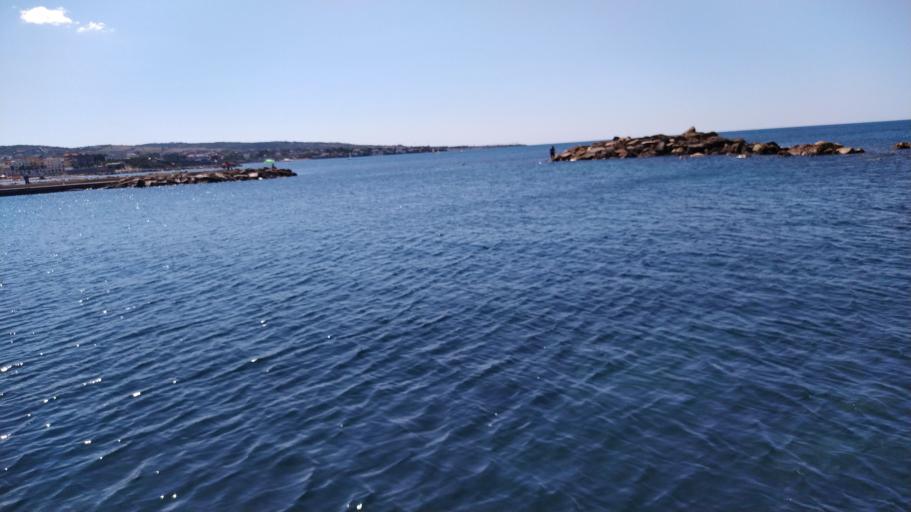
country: IT
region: Latium
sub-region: Citta metropolitana di Roma Capitale
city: Civitavecchia
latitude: 42.0889
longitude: 11.7912
